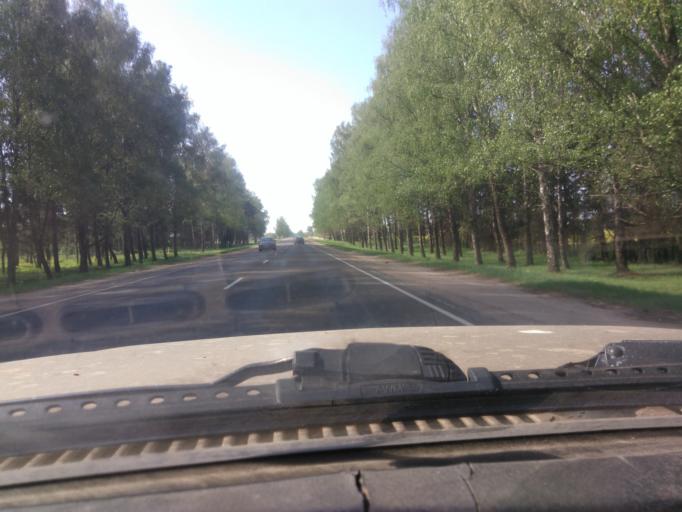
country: BY
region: Mogilev
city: Buynichy
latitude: 53.8432
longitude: 30.2496
